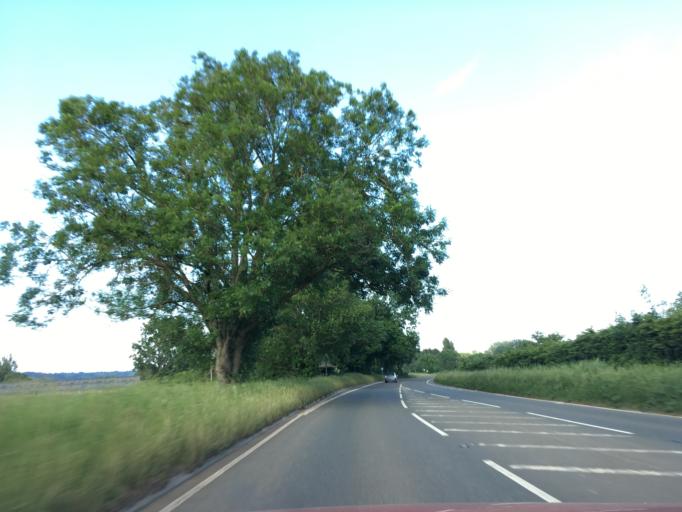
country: GB
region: England
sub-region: North Somerset
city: Churchill
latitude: 51.3397
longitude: -2.7795
